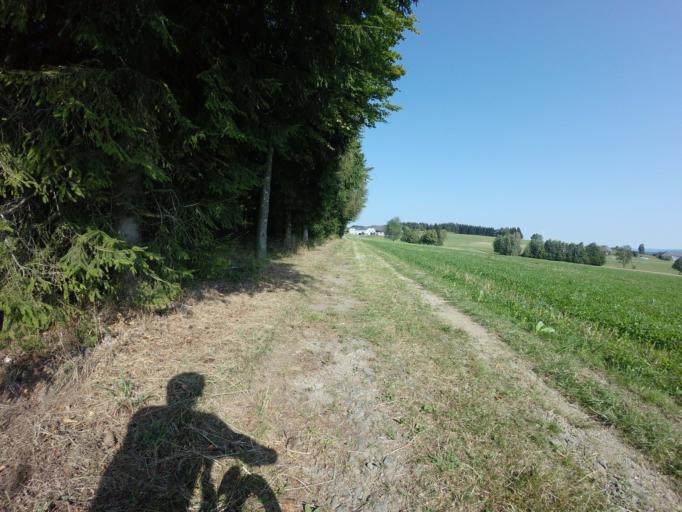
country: AT
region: Upper Austria
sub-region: Politischer Bezirk Urfahr-Umgebung
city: Bad Leonfelden
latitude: 48.5515
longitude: 14.3211
